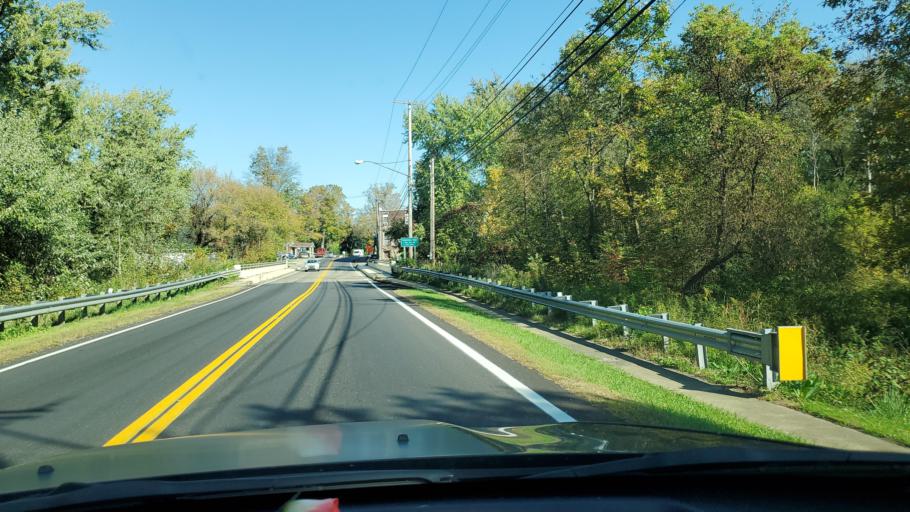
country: US
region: Ohio
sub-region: Ashtabula County
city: Andover
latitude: 41.4424
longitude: -80.5883
